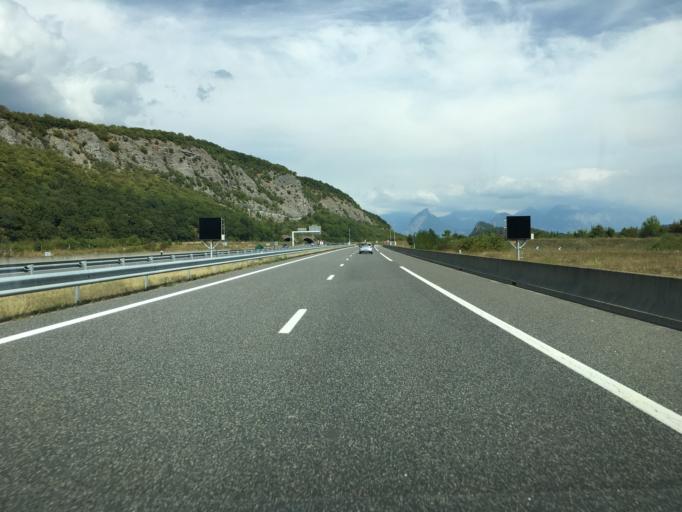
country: FR
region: Rhone-Alpes
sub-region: Departement de l'Isere
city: Vif
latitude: 45.0751
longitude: 5.6797
